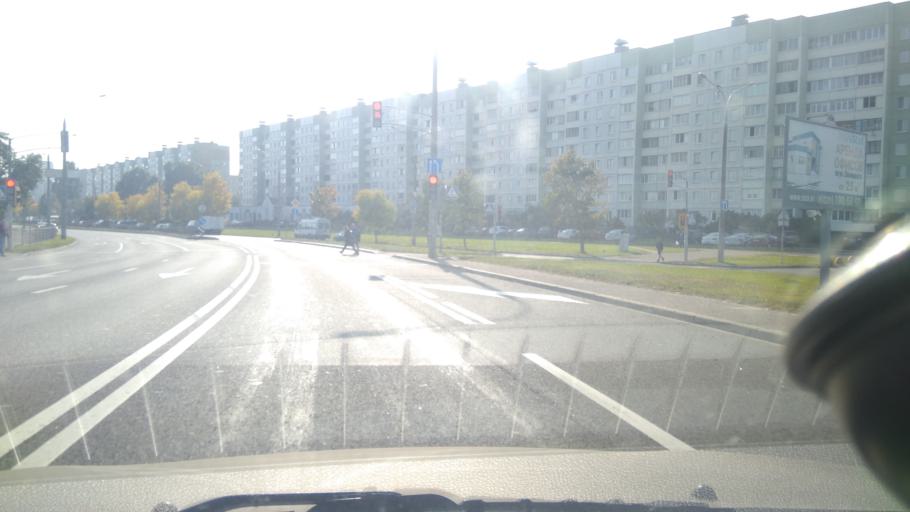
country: BY
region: Minsk
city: Vyaliki Trastsyanets
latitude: 53.8451
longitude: 27.7078
